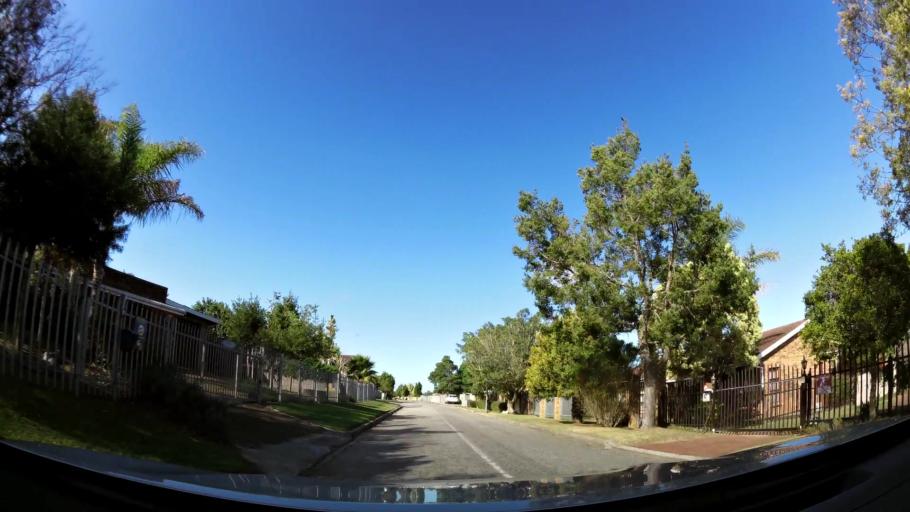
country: ZA
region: Western Cape
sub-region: Eden District Municipality
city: George
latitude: -33.9676
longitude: 22.4937
